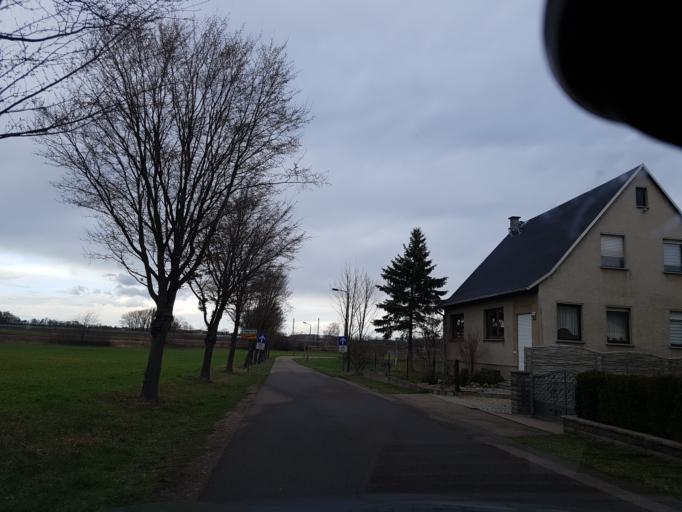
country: DE
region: Saxony
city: Stauchitz
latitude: 51.2671
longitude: 13.2388
